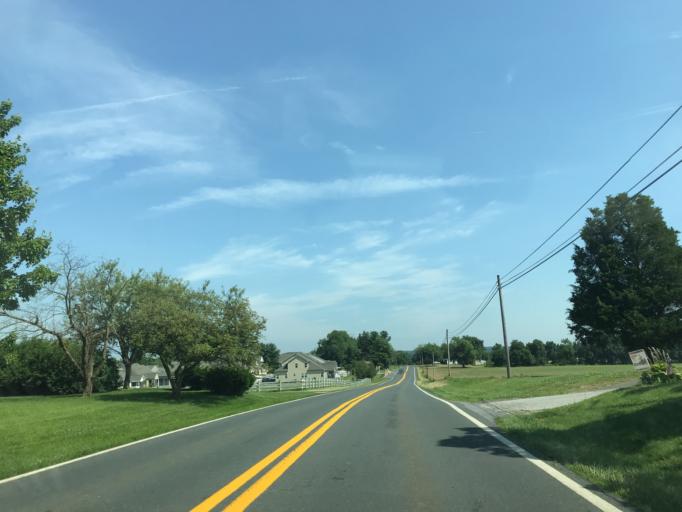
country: US
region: Maryland
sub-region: Carroll County
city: Taneytown
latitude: 39.6399
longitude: -77.1602
